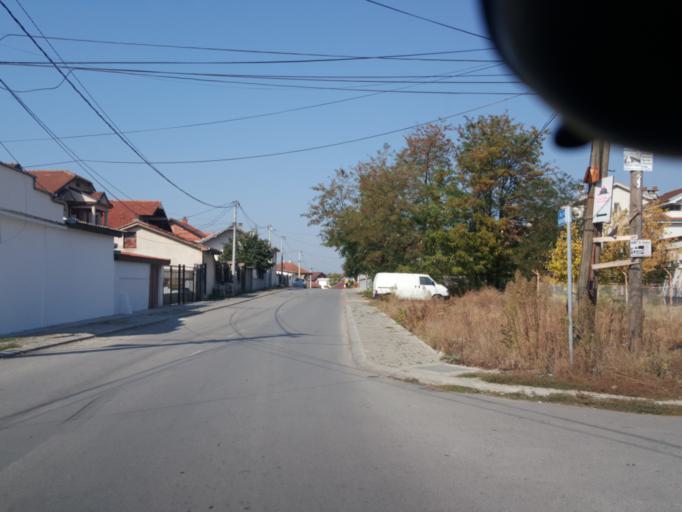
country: XK
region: Gjakova
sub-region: Komuna e Gjakoves
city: Gjakove
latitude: 42.3920
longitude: 20.4293
